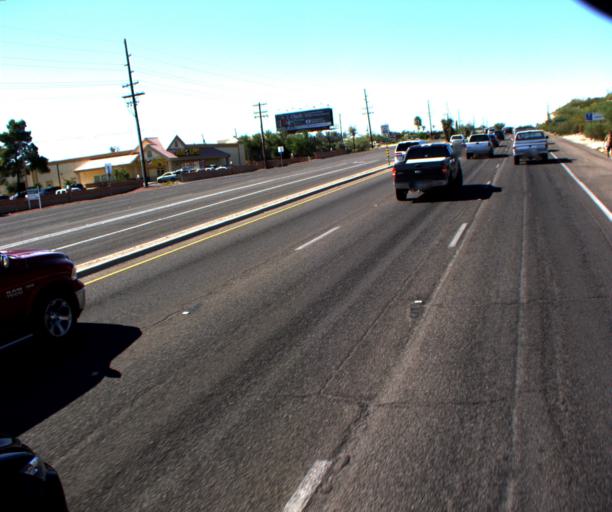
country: US
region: Arizona
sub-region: Pima County
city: Casas Adobes
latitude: 32.2983
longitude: -110.9782
